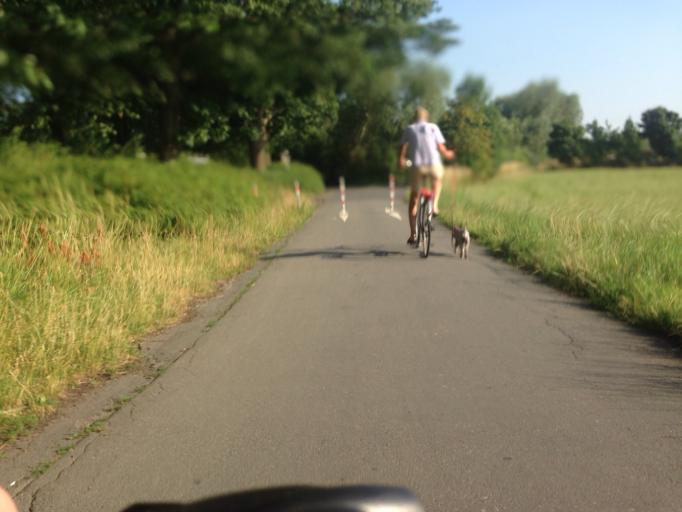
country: DE
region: North Rhine-Westphalia
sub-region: Regierungsbezirk Munster
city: Muenster
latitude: 51.9796
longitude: 7.6066
